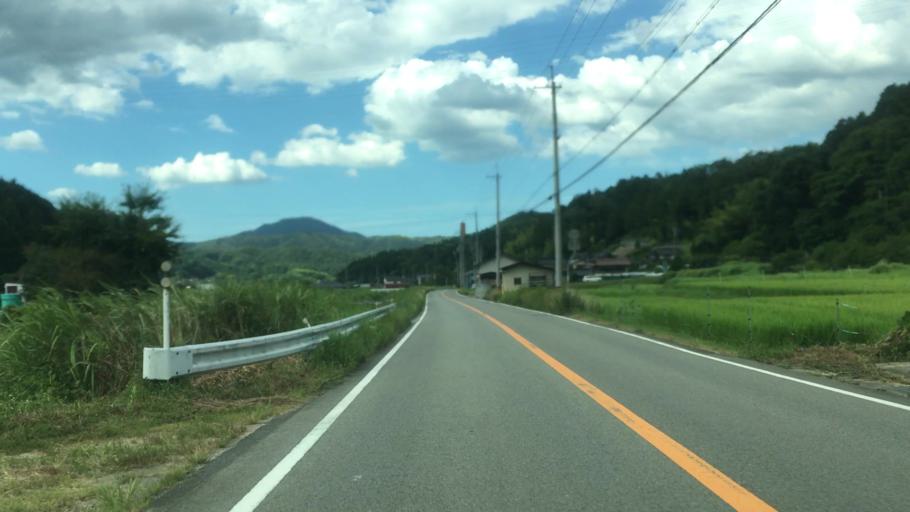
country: JP
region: Hyogo
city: Toyooka
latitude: 35.5374
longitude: 134.7898
